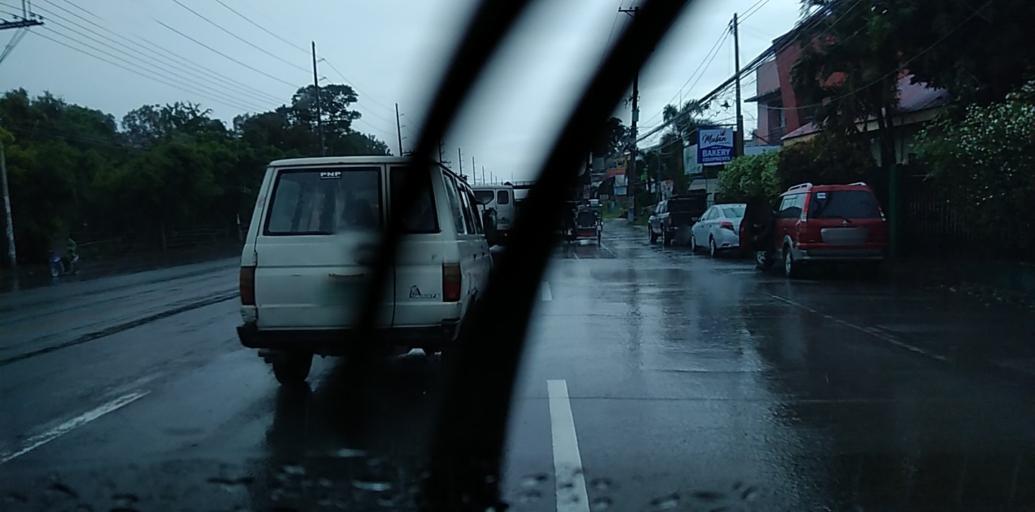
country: PH
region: Central Luzon
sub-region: Province of Pampanga
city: Magliman
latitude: 15.0579
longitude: 120.6579
